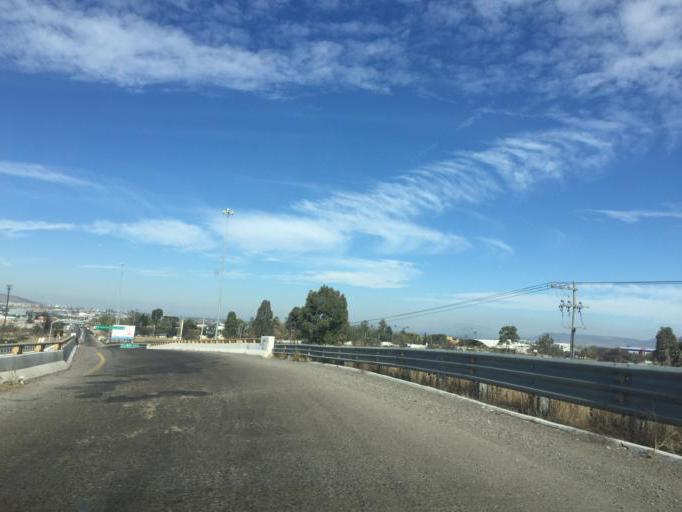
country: MX
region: Queretaro
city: San Juan del Rio
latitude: 20.3704
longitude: -99.9844
